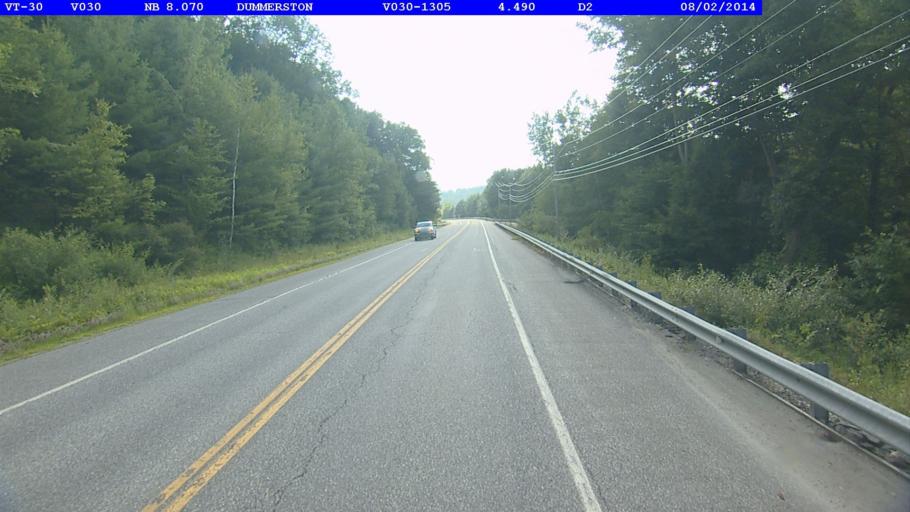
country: US
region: Vermont
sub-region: Windham County
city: Newfane
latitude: 42.9478
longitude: -72.6298
